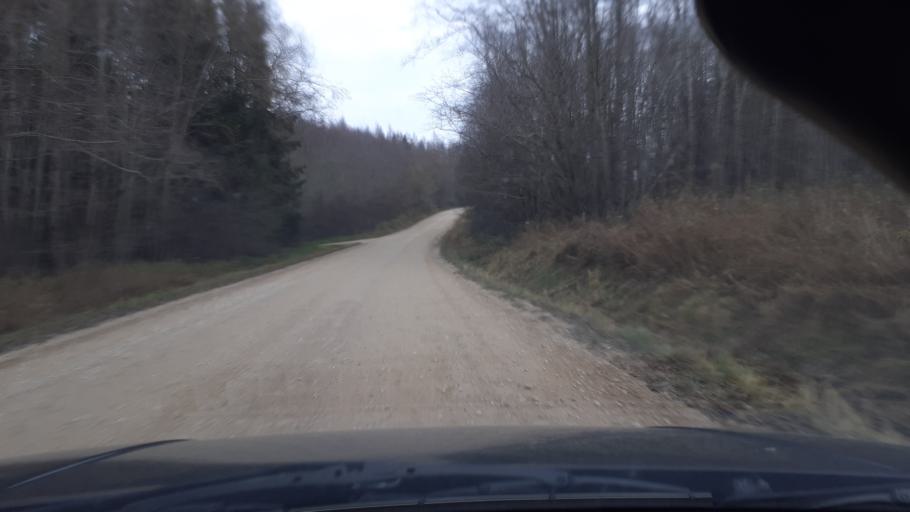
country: LV
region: Alsunga
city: Alsunga
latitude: 56.9562
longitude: 21.6496
